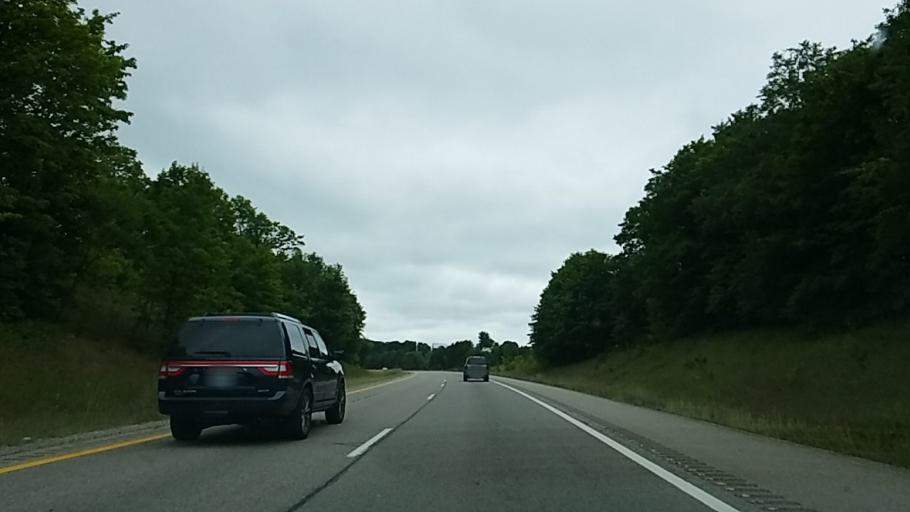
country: US
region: Michigan
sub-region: Otsego County
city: Gaylord
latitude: 45.0826
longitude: -84.6915
